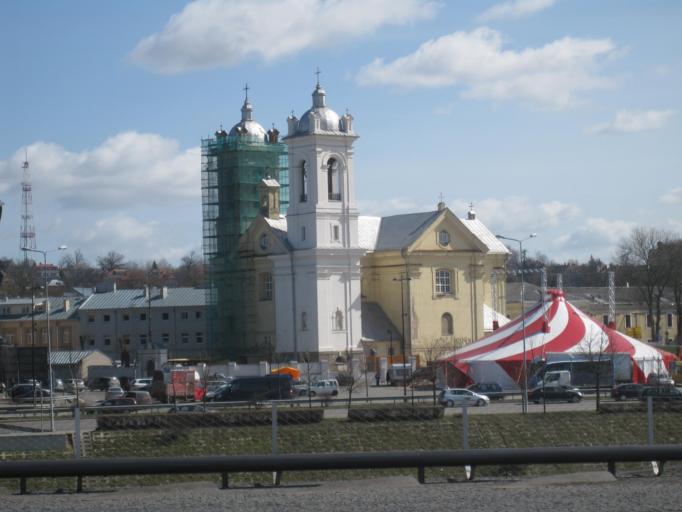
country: LT
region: Kauno apskritis
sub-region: Kaunas
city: Aleksotas
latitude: 54.8891
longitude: 23.9178
